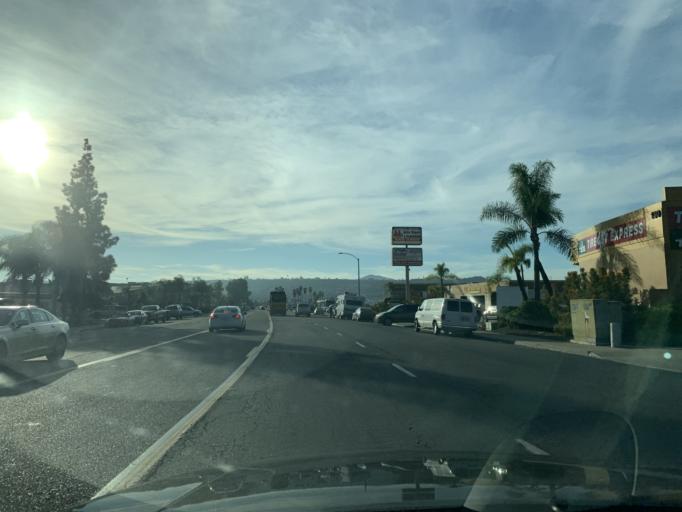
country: US
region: California
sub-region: San Diego County
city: Santee
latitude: 32.8191
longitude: -116.9632
